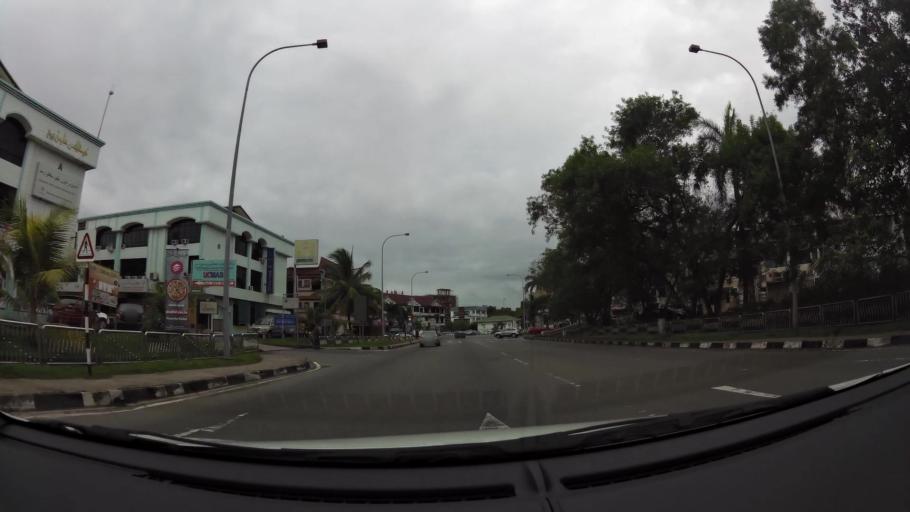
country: BN
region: Brunei and Muara
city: Bandar Seri Begawan
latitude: 4.9011
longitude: 114.9283
